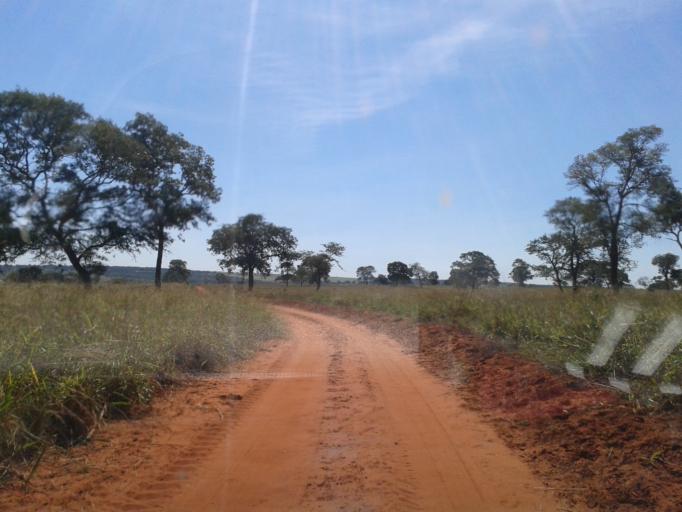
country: BR
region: Minas Gerais
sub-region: Santa Vitoria
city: Santa Vitoria
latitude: -19.0155
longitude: -50.3242
